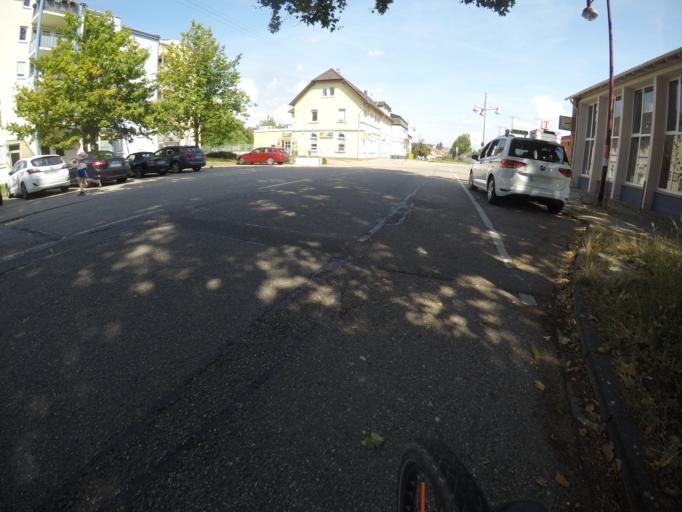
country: DE
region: Baden-Wuerttemberg
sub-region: Karlsruhe Region
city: Bretten
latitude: 49.0374
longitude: 8.6936
